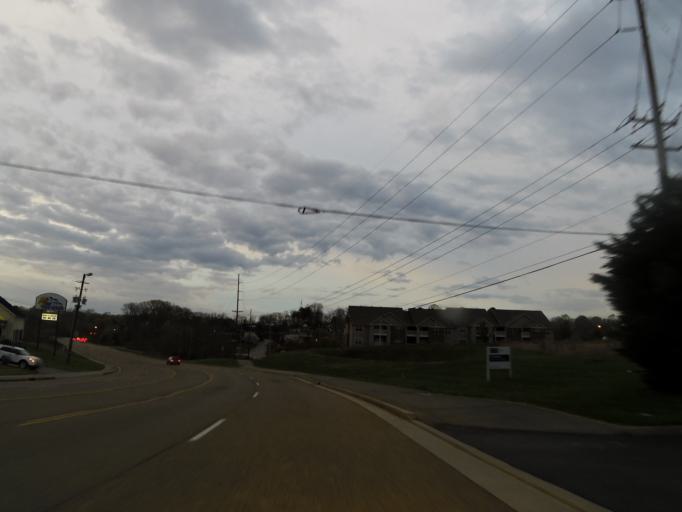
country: US
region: Tennessee
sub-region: Knox County
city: Farragut
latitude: 35.9280
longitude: -84.0588
